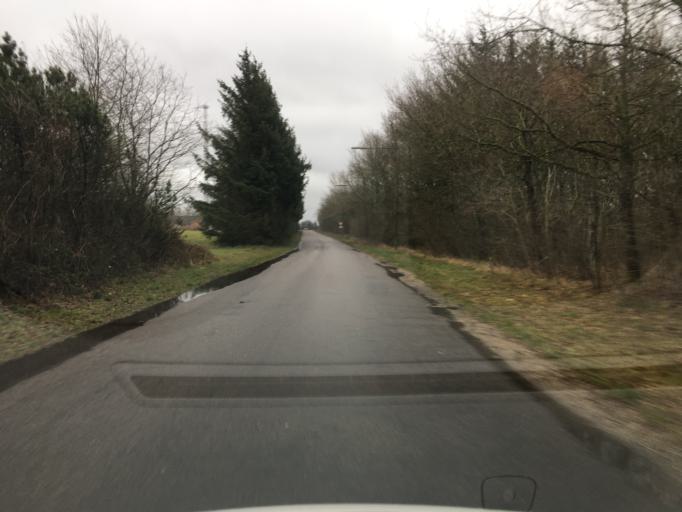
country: DK
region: South Denmark
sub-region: Aabenraa Kommune
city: Tinglev
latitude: 54.9287
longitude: 9.2283
